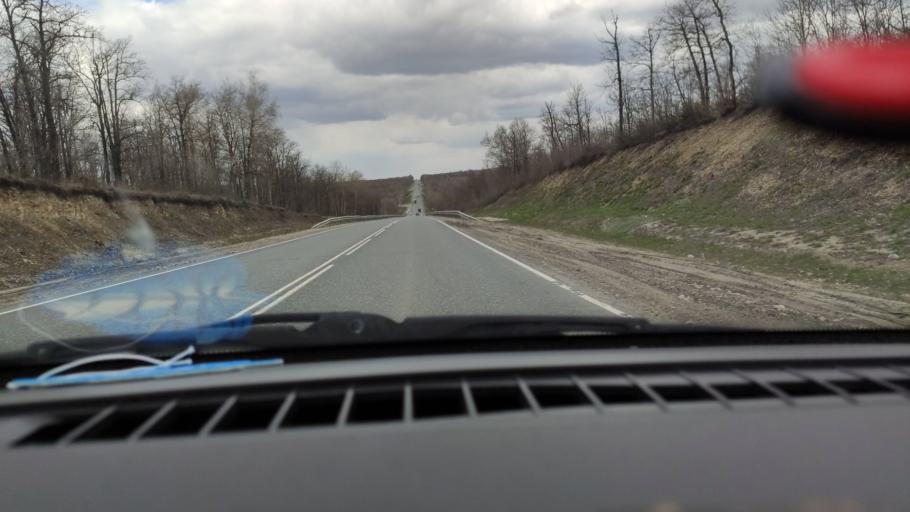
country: RU
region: Saratov
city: Vol'sk
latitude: 52.1087
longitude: 47.3854
